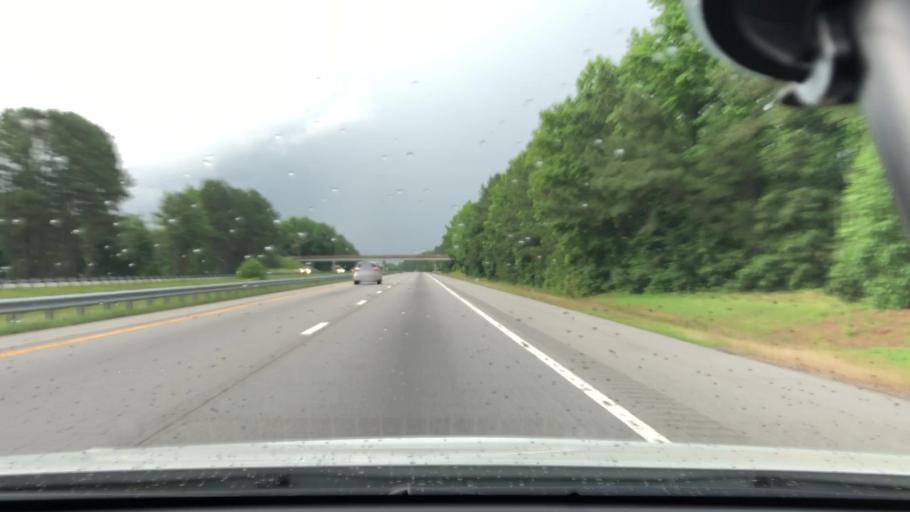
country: US
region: North Carolina
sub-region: Halifax County
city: Enfield
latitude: 36.2890
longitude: -77.7145
